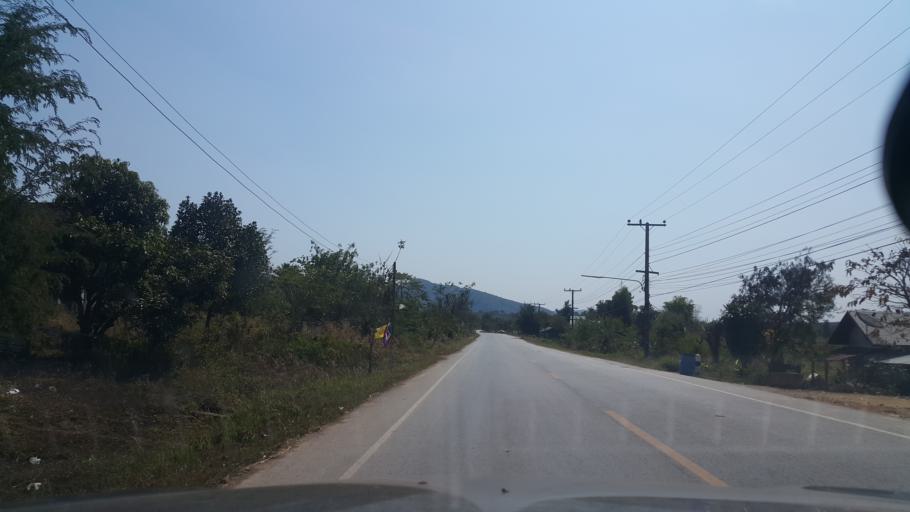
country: TH
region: Changwat Udon Thani
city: Na Yung
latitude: 17.8813
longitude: 102.0865
